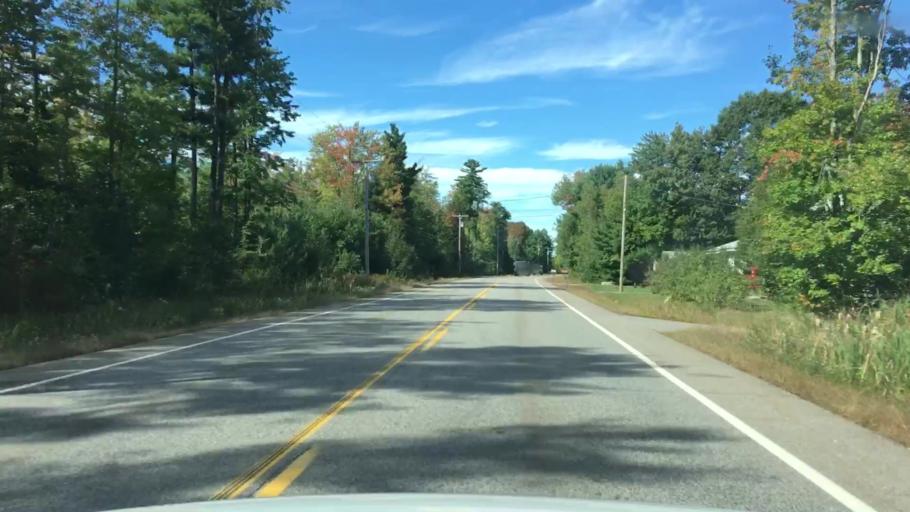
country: US
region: Maine
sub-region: Cumberland County
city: Westbrook
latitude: 43.6518
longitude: -70.3980
